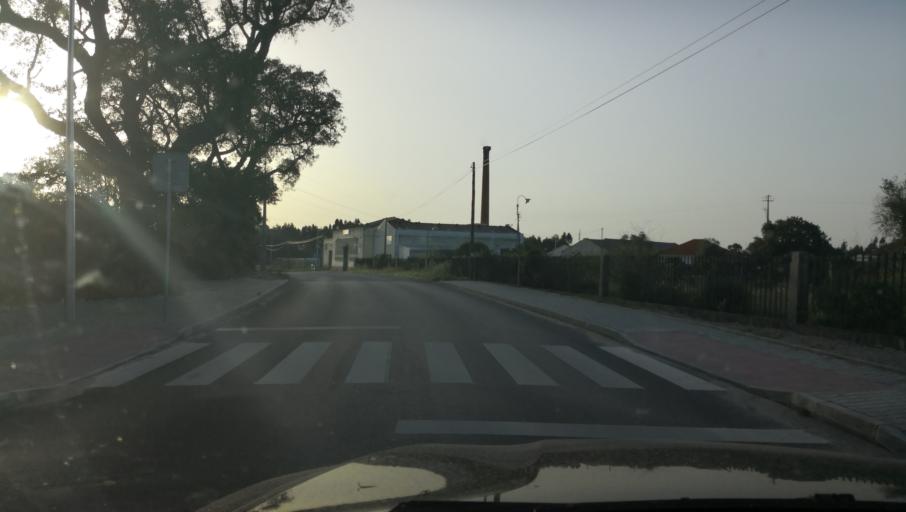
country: PT
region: Setubal
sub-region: Setubal
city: Setubal
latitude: 38.5381
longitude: -8.8291
